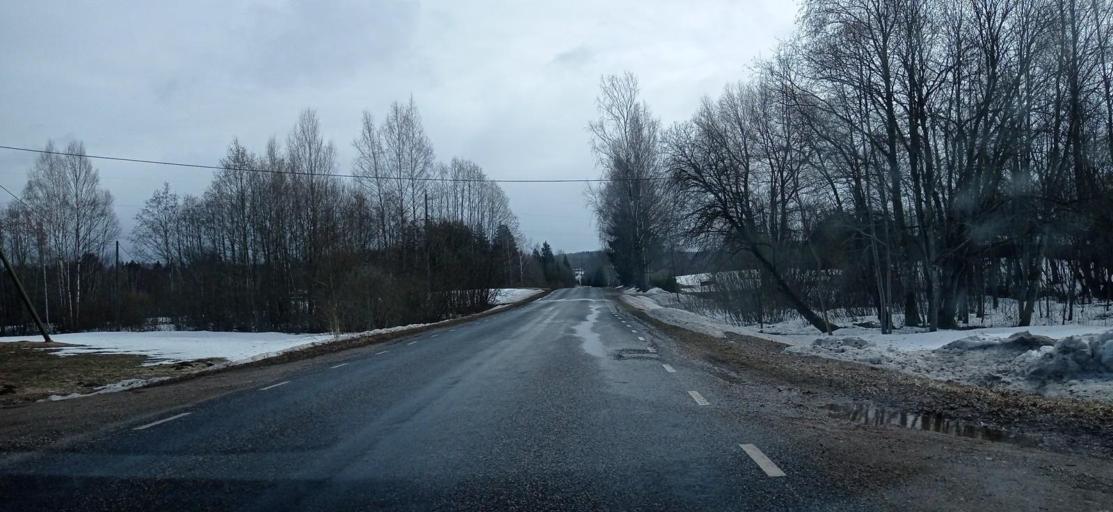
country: EE
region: Tartu
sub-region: UElenurme vald
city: Ulenurme
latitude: 58.0708
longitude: 26.7098
